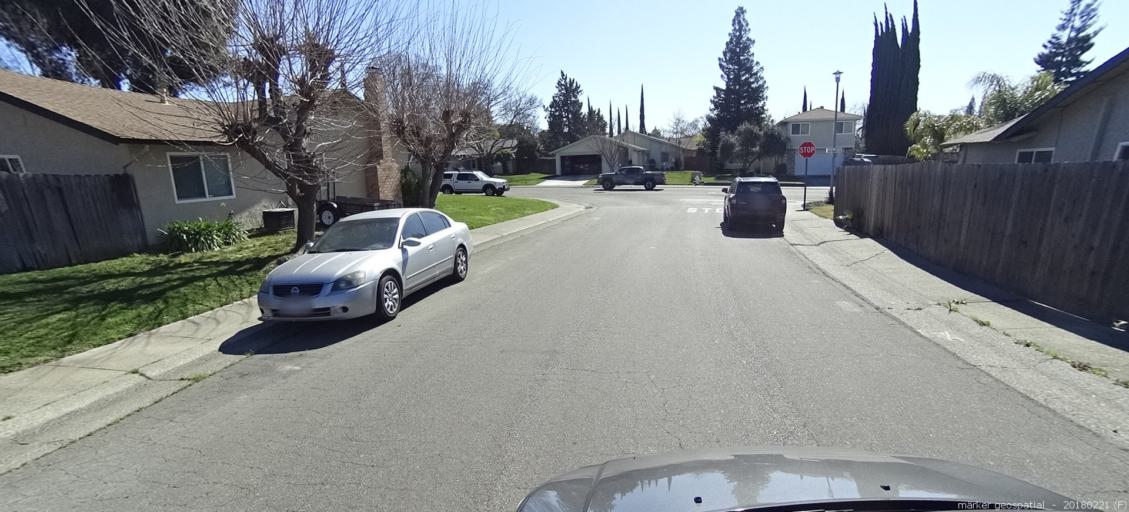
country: US
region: California
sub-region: Sacramento County
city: Orangevale
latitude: 38.6909
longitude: -121.2464
